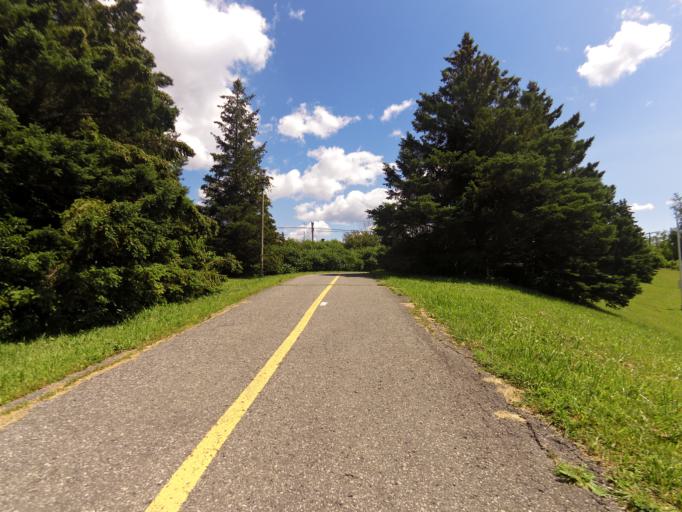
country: CA
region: Ontario
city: Ottawa
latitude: 45.3749
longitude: -75.6819
